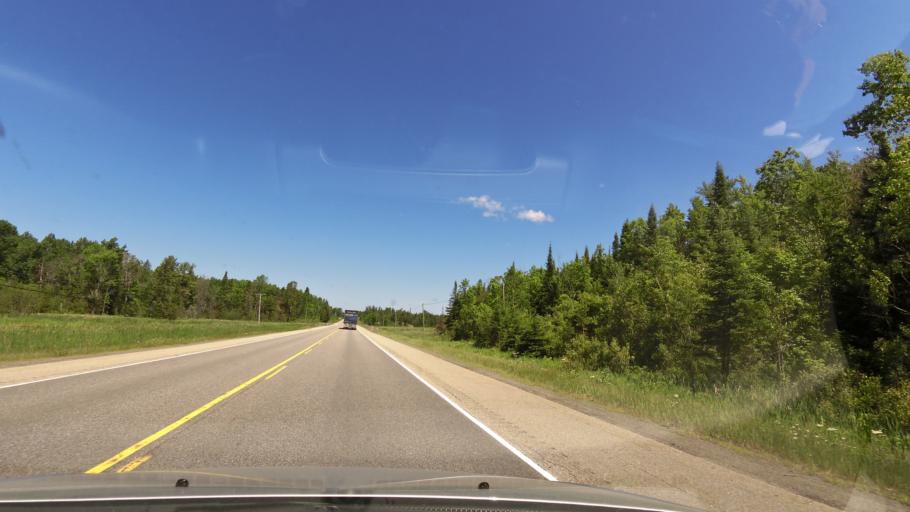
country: CA
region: Ontario
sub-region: Parry Sound District
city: Parry Sound
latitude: 45.8666
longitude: -80.5666
